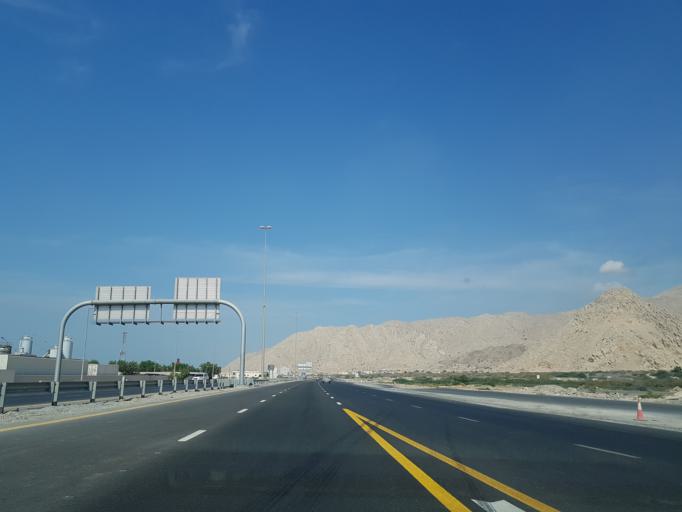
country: AE
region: Ra's al Khaymah
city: Ras al-Khaimah
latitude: 25.8382
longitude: 56.0166
